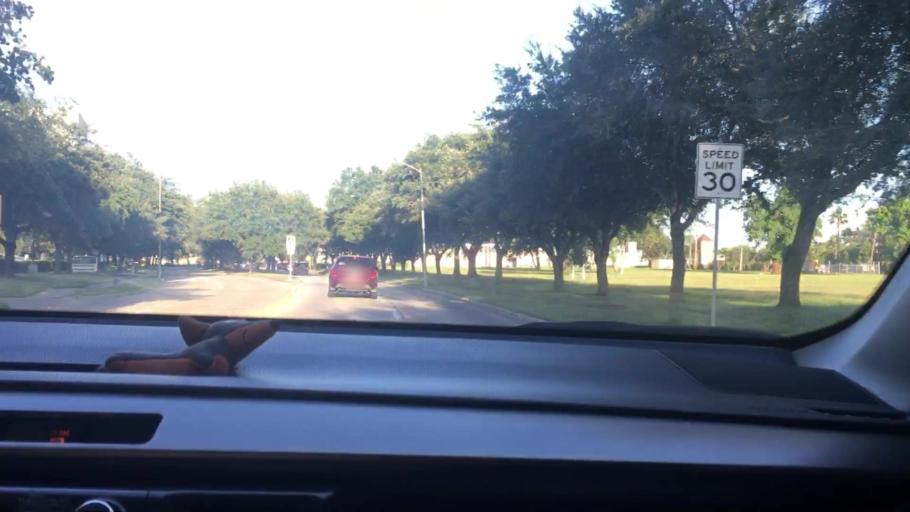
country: US
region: Texas
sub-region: Fort Bend County
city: Meadows Place
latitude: 29.6433
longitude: -95.5846
